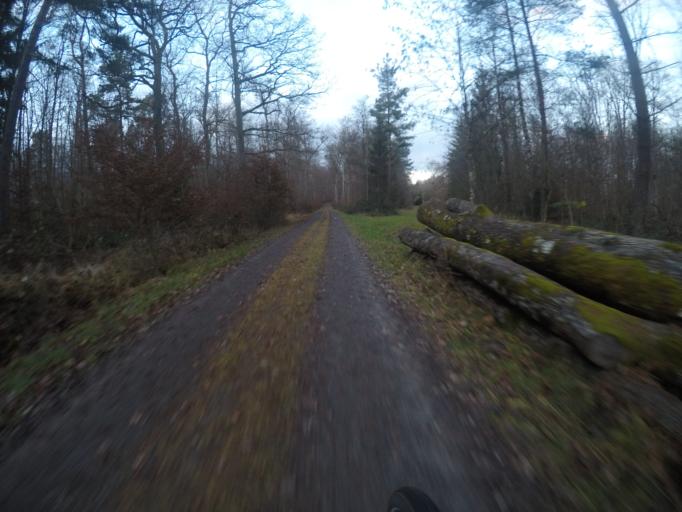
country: DE
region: Baden-Wuerttemberg
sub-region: Tuebingen Region
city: Dettenhausen
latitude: 48.5733
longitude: 9.1062
